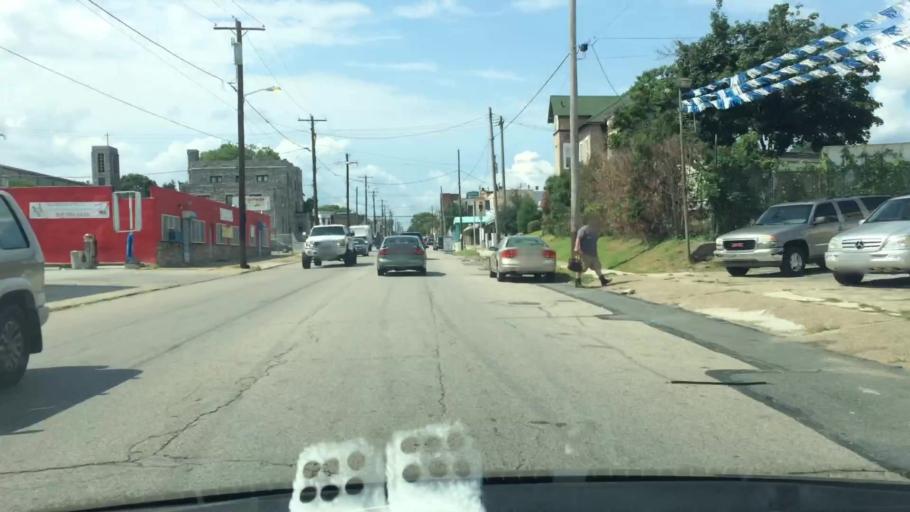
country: US
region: Pennsylvania
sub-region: Delaware County
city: Colwyn
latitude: 39.9218
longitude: -75.2250
